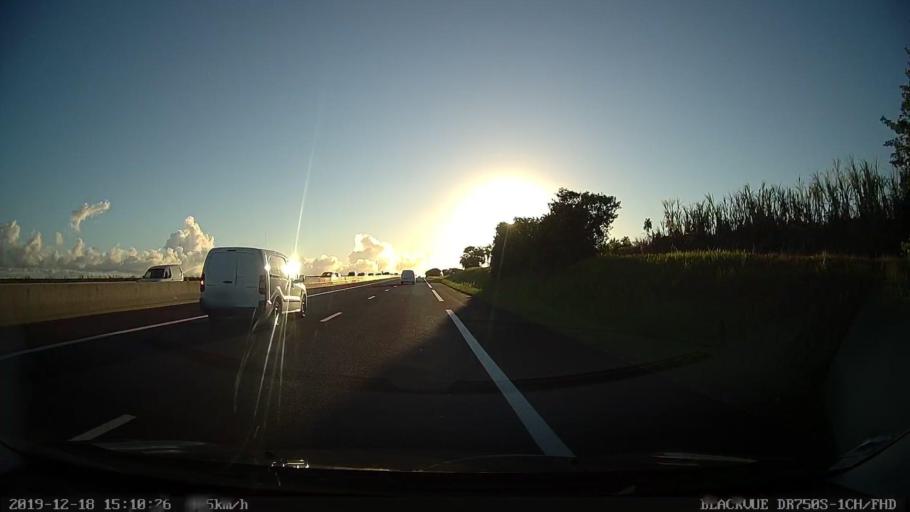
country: RE
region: Reunion
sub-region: Reunion
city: Sainte-Suzanne
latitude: -20.9008
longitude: 55.5875
